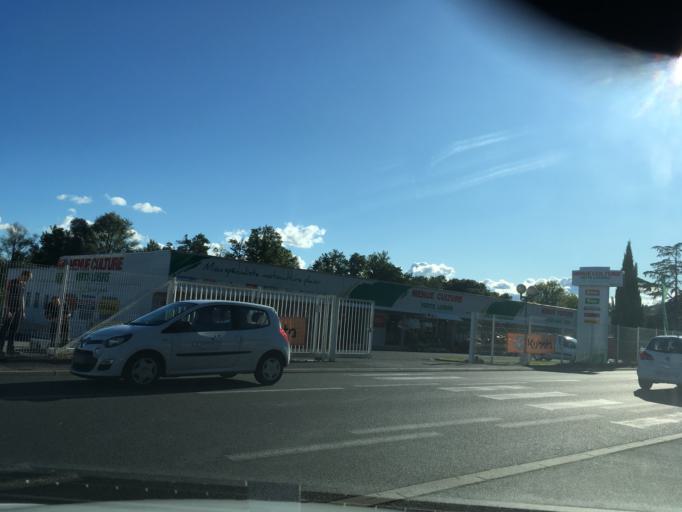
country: FR
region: Limousin
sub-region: Departement de la Correze
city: Ussac
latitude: 45.1648
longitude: 1.4940
